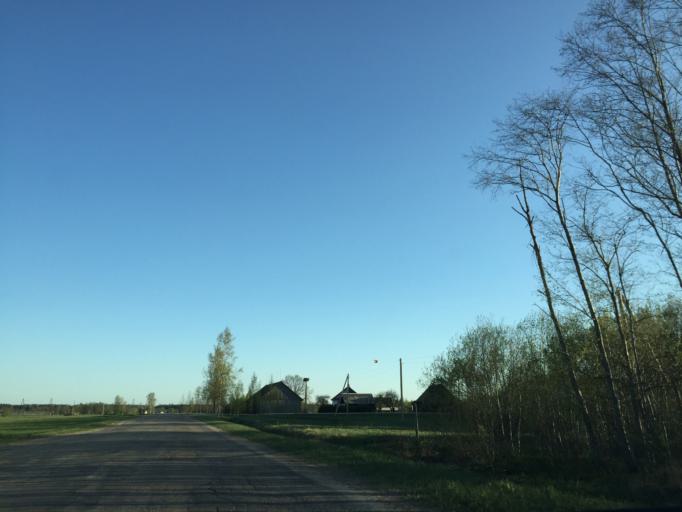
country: LV
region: Koknese
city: Koknese
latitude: 56.6896
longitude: 25.4870
